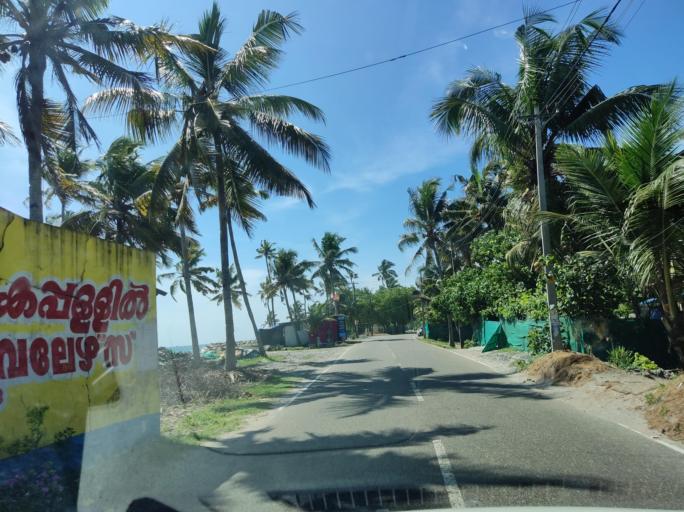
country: IN
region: Kerala
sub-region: Alappuzha
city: Kayankulam
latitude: 9.1979
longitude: 76.4352
